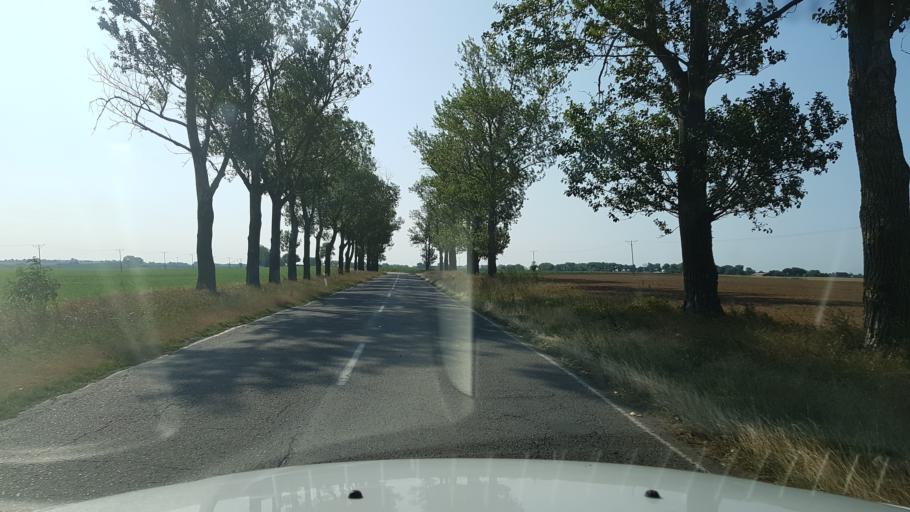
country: PL
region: West Pomeranian Voivodeship
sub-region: Powiat stargardzki
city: Stargard Szczecinski
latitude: 53.2685
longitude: 15.0892
